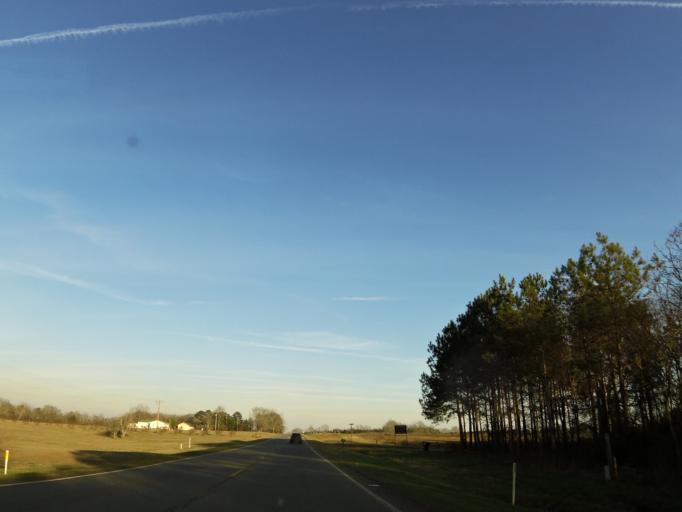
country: US
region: Georgia
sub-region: Sumter County
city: Americus
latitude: 32.0476
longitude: -84.3599
